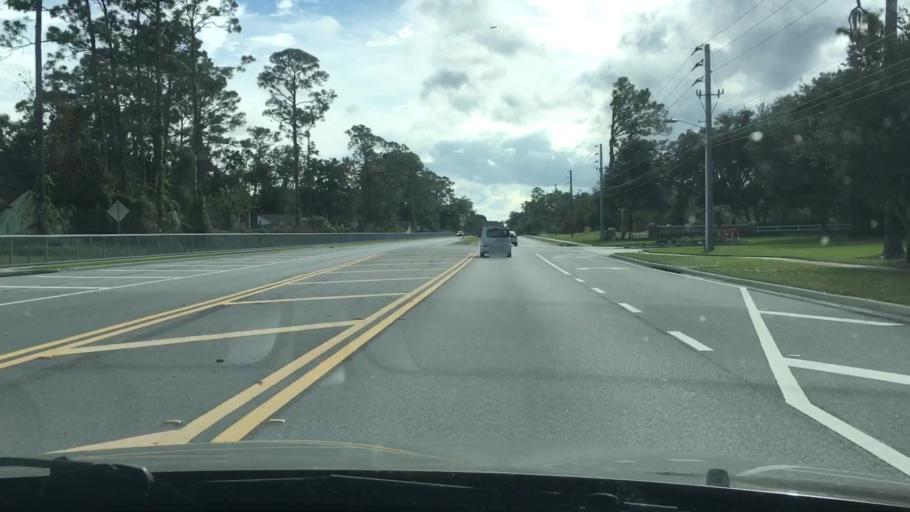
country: US
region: Florida
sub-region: Volusia County
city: Ormond Beach
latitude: 29.2645
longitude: -81.1293
